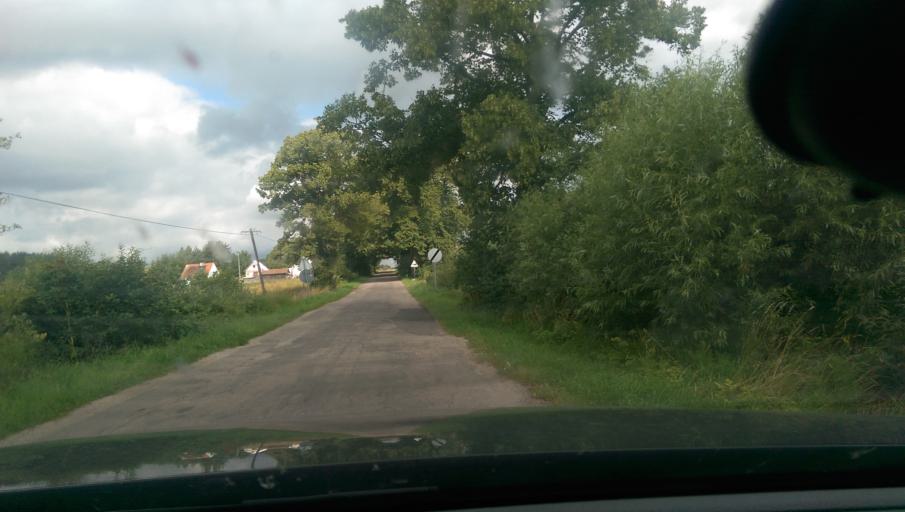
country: PL
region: Warmian-Masurian Voivodeship
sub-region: Powiat wegorzewski
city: Pozezdrze
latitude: 54.1895
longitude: 21.9166
